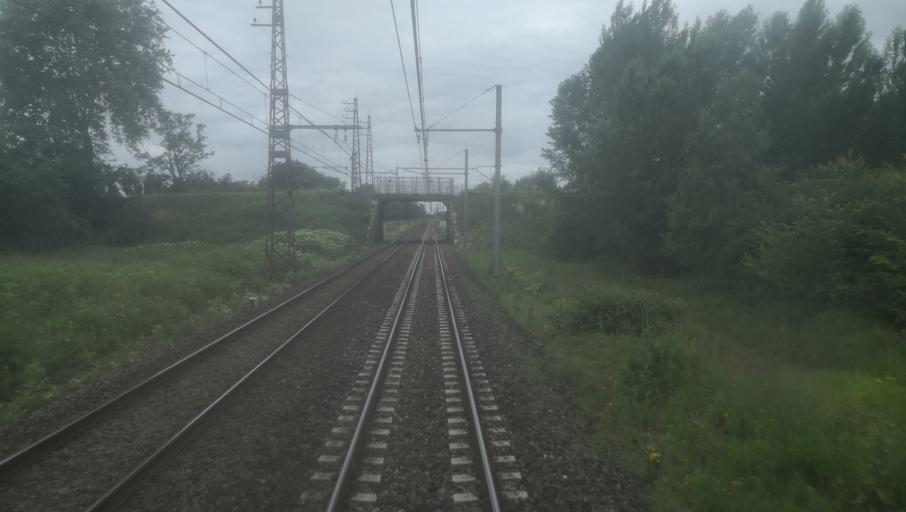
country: FR
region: Midi-Pyrenees
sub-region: Departement du Tarn-et-Garonne
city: Grisolles
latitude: 43.8384
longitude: 1.2948
